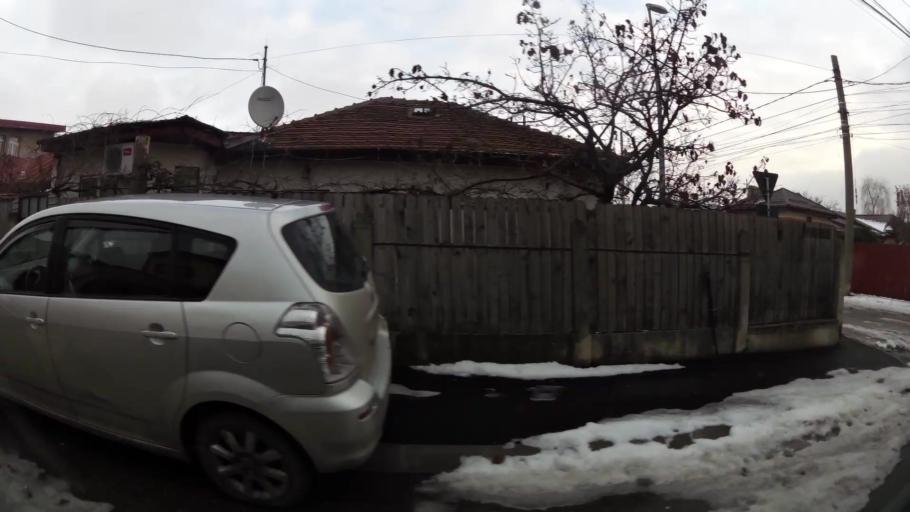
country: RO
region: Ilfov
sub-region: Voluntari City
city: Voluntari
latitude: 44.4842
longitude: 26.1877
